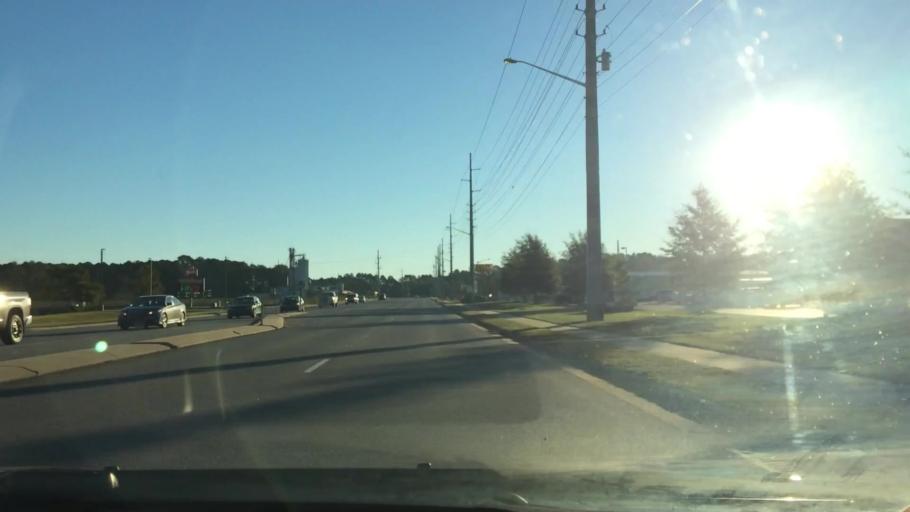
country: US
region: North Carolina
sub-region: Pitt County
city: Winterville
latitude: 35.5482
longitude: -77.3993
